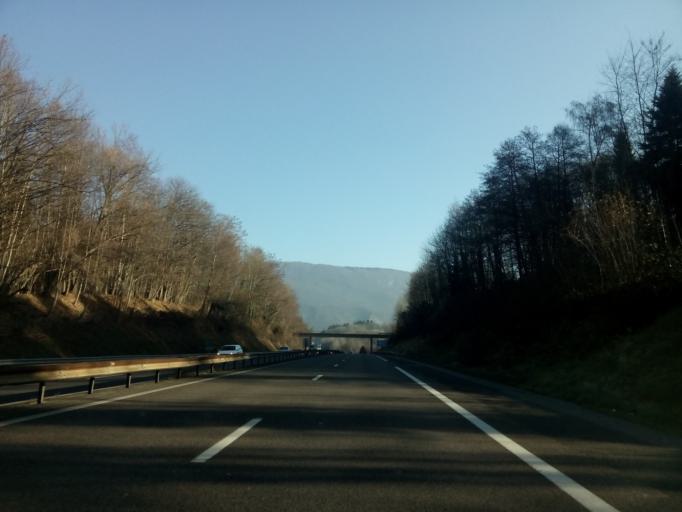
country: FR
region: Rhone-Alpes
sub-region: Departement de la Savoie
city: Novalaise
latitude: 45.5630
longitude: 5.7697
